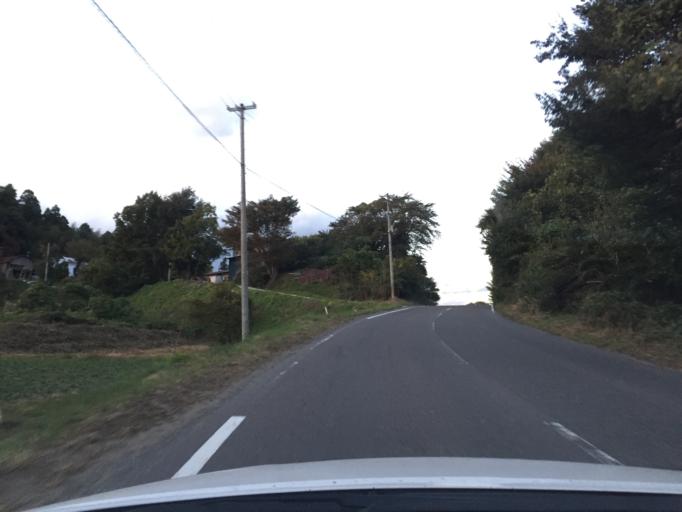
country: JP
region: Fukushima
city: Miharu
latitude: 37.4673
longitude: 140.4401
